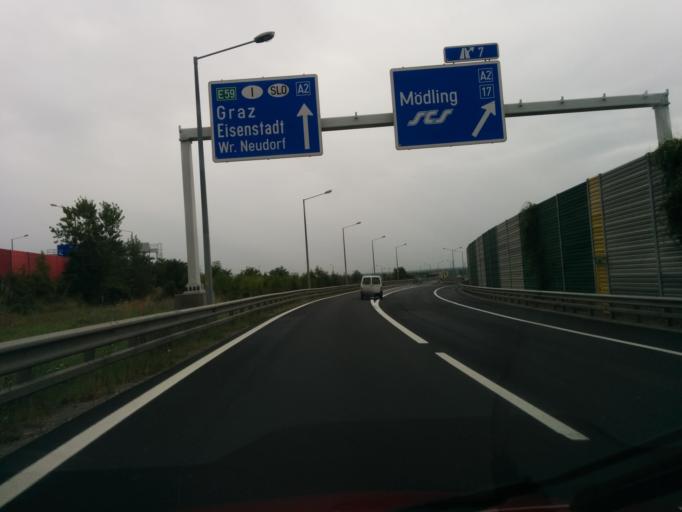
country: AT
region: Lower Austria
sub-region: Politischer Bezirk Modling
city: Vosendorf
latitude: 48.1205
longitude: 16.3200
